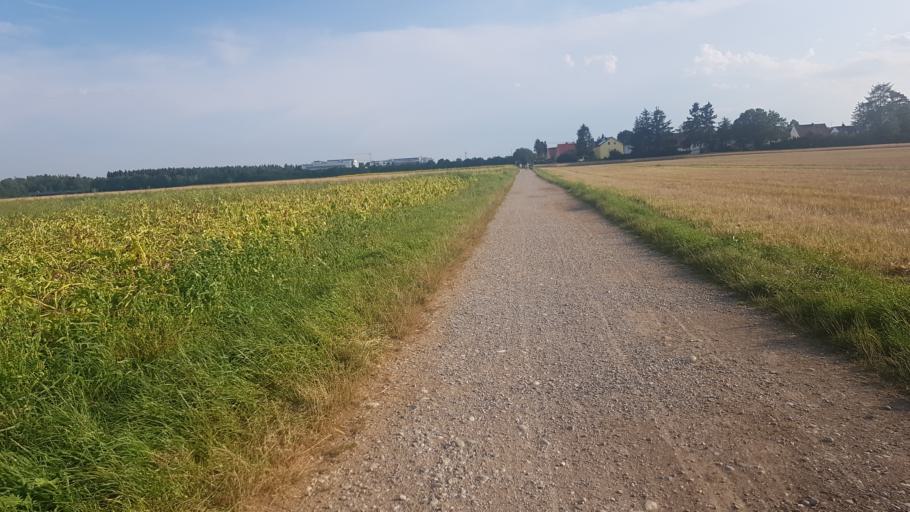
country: DE
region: Bavaria
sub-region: Upper Bavaria
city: Pasing
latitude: 48.1321
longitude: 11.4543
